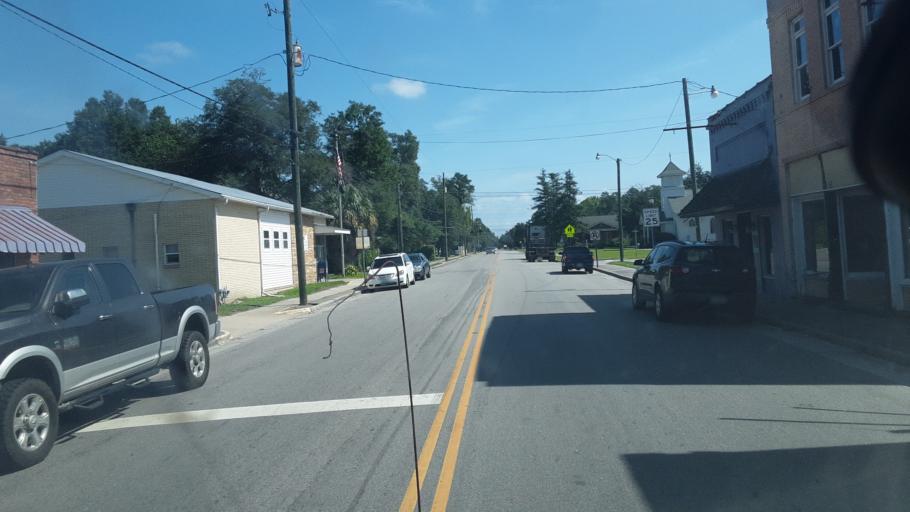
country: US
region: South Carolina
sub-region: Hampton County
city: Varnville
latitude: 32.8507
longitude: -81.0799
